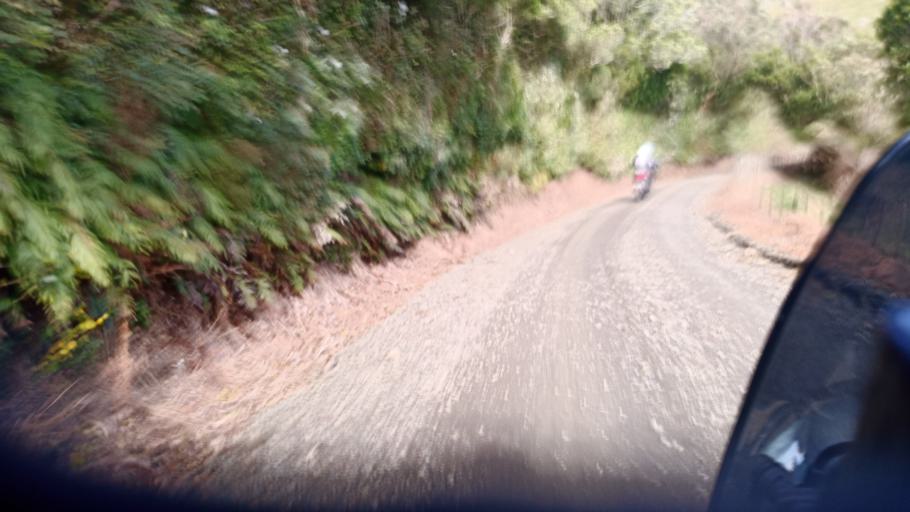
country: NZ
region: Gisborne
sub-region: Gisborne District
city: Gisborne
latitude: -38.4628
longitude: 177.5364
